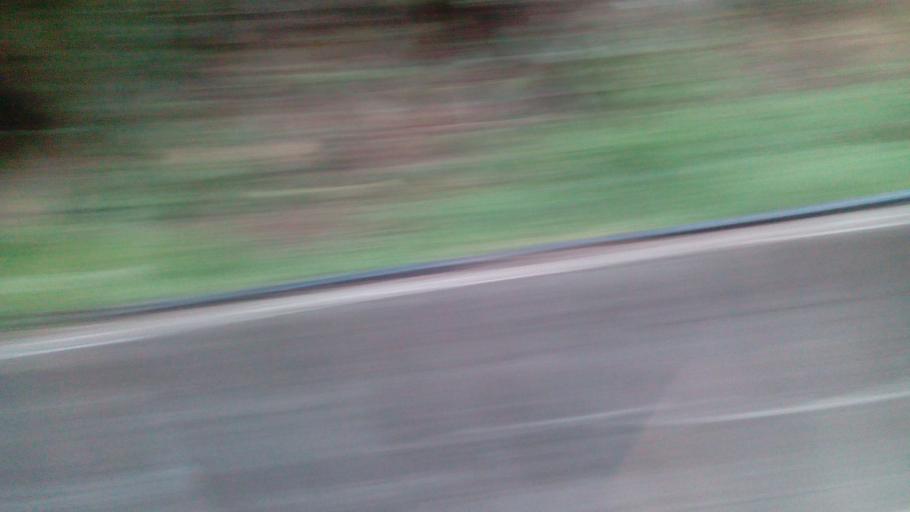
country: TW
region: Taiwan
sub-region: Hualien
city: Hualian
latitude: 24.3272
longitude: 121.2968
